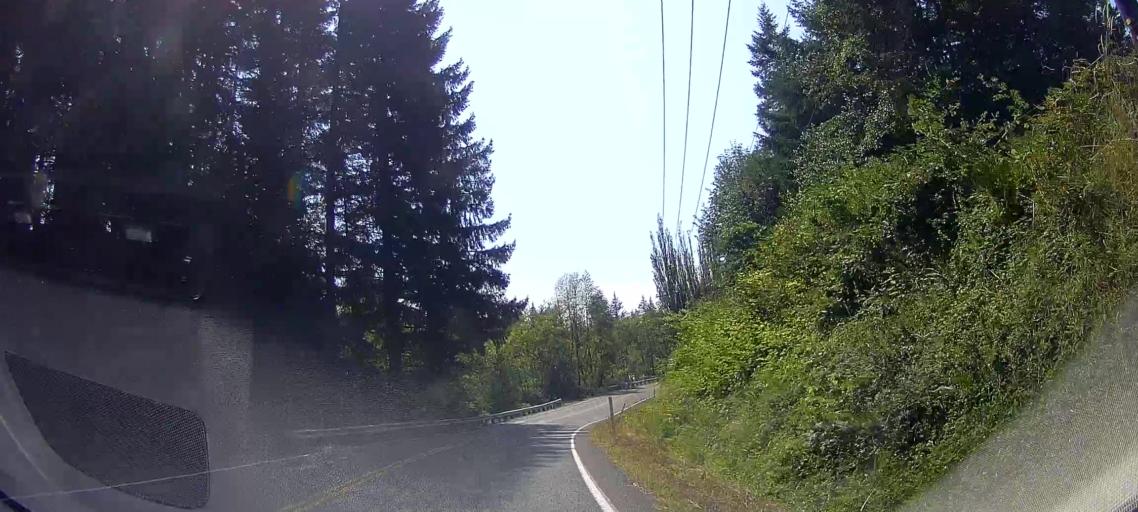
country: US
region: Washington
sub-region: Snohomish County
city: Bryant
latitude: 48.3269
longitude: -122.1416
